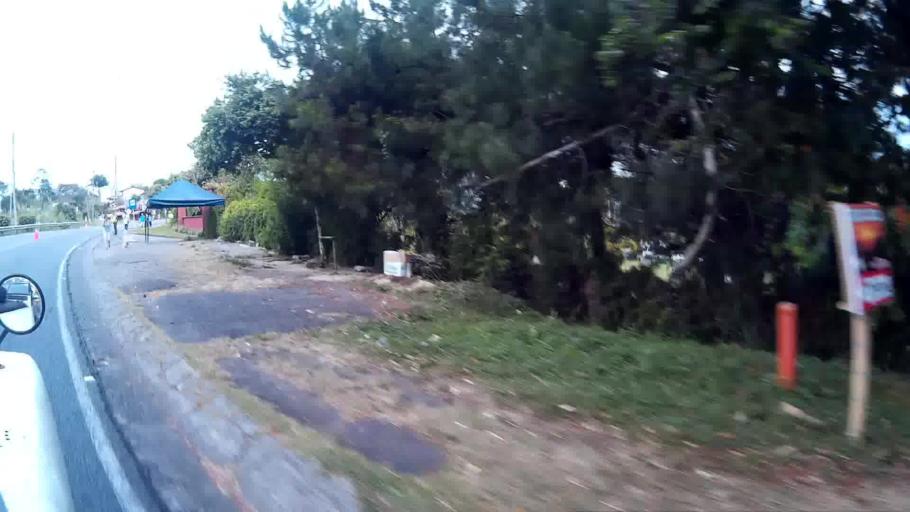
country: CO
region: Risaralda
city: Pereira
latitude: 4.7573
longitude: -75.6782
